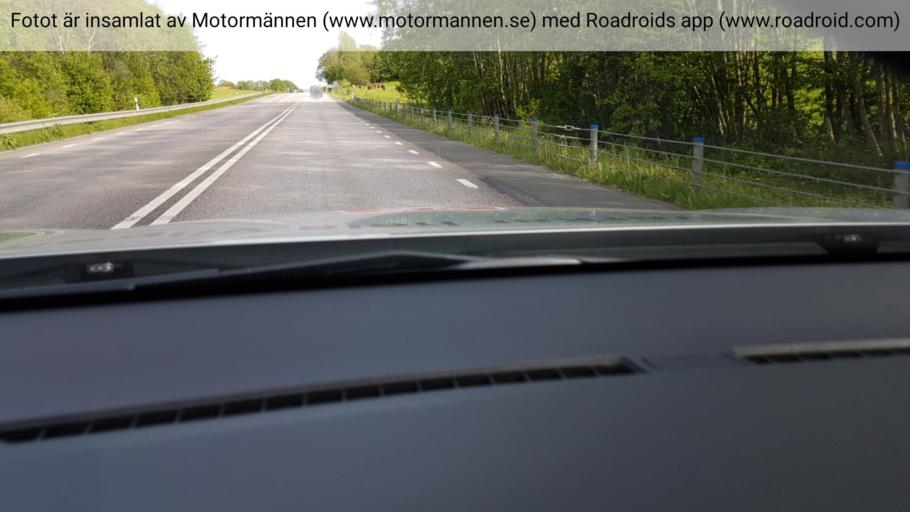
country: SE
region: Vaestra Goetaland
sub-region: Skovde Kommun
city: Skoevde
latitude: 58.3848
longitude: 13.8030
